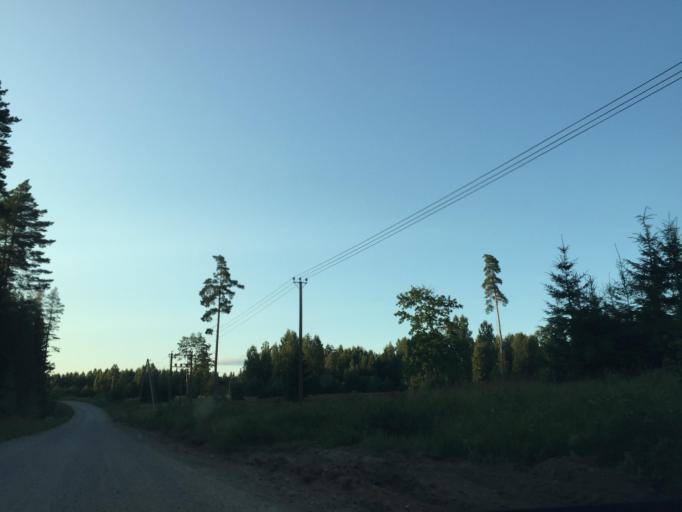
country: LV
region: Kuldigas Rajons
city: Kuldiga
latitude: 57.1159
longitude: 22.2137
